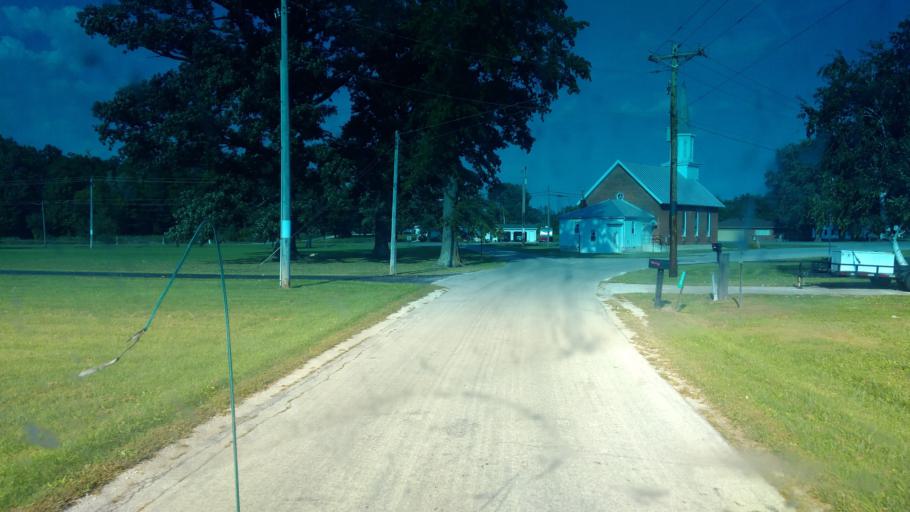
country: US
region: Ohio
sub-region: Wyandot County
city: Carey
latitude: 40.9198
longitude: -83.3479
